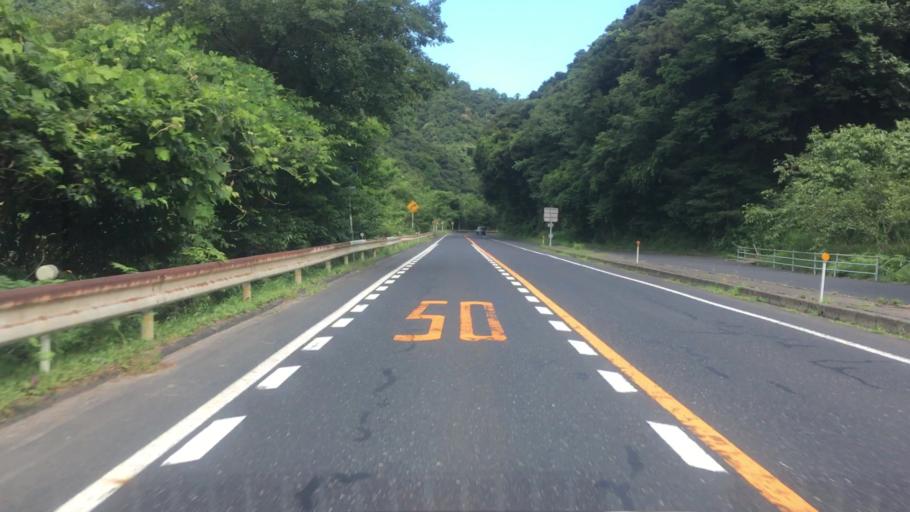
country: JP
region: Tottori
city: Tottori
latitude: 35.5947
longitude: 134.3535
